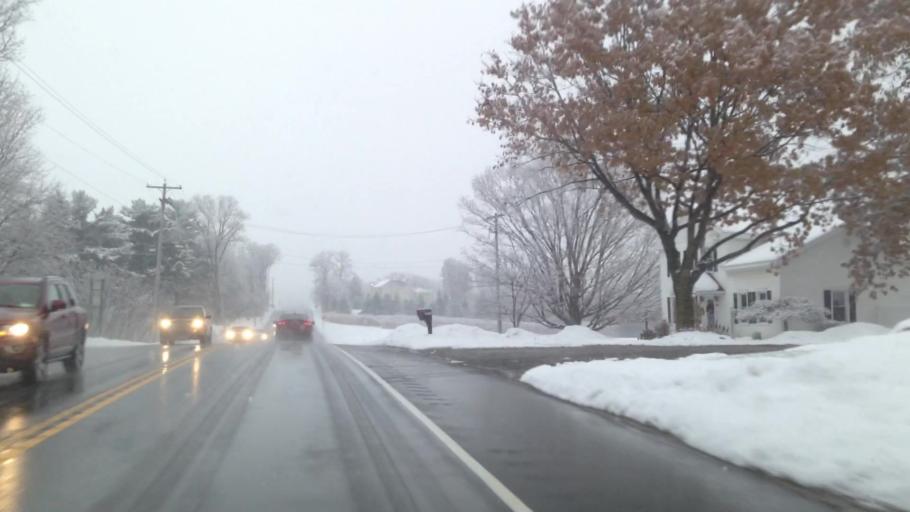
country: US
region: New York
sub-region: Onondaga County
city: Peru
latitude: 43.0342
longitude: -76.3765
